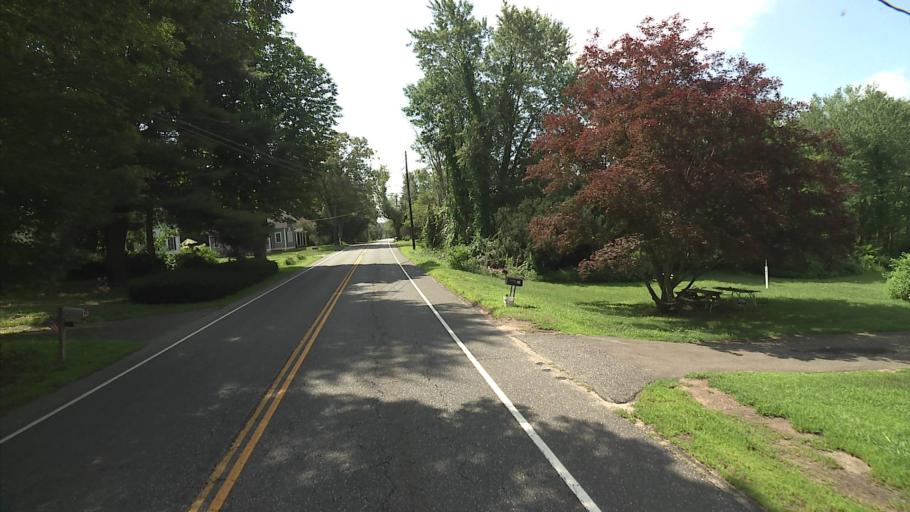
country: US
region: Connecticut
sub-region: Middlesex County
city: Deep River Center
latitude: 41.3667
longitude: -72.4505
